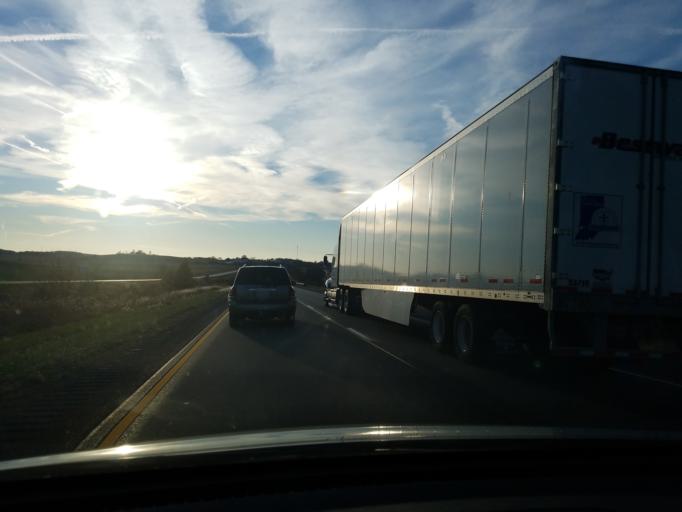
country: US
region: Indiana
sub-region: Dubois County
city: Ferdinand
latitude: 38.2042
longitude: -86.8993
